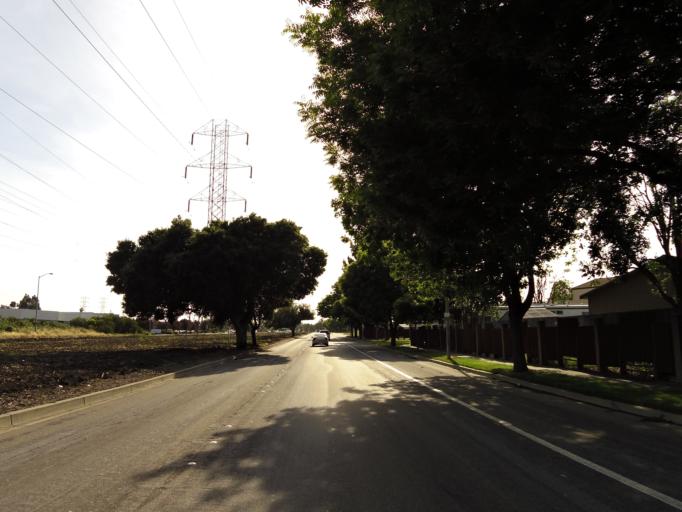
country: US
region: California
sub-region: Alameda County
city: Fremont
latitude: 37.5111
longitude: -121.9556
